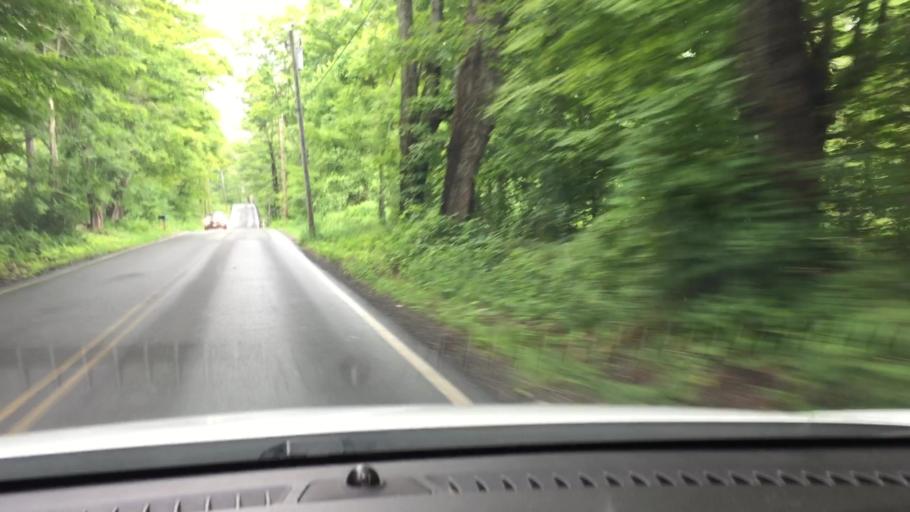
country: US
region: Massachusetts
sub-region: Berkshire County
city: Hinsdale
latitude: 42.4480
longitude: -73.1452
